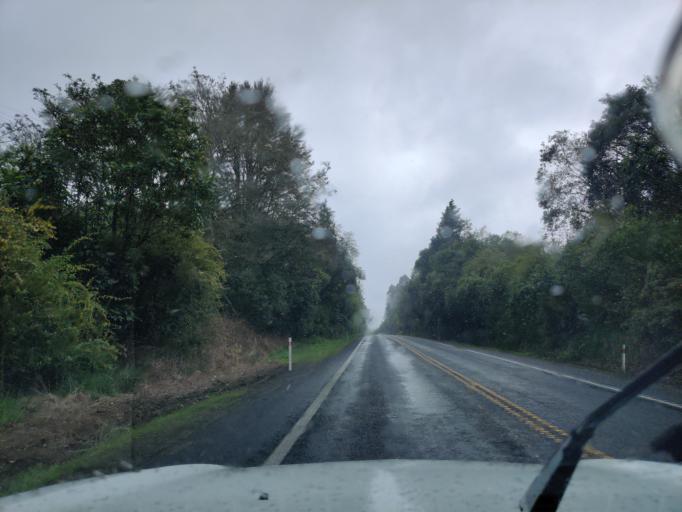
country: NZ
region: Bay of Plenty
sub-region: Rotorua District
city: Rotorua
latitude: -38.0815
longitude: 176.1866
